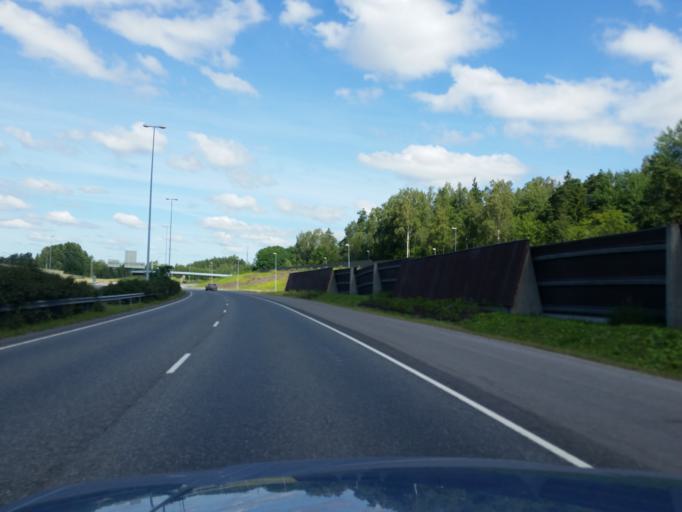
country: FI
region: Uusimaa
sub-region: Helsinki
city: Kauniainen
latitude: 60.1893
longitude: 24.7480
